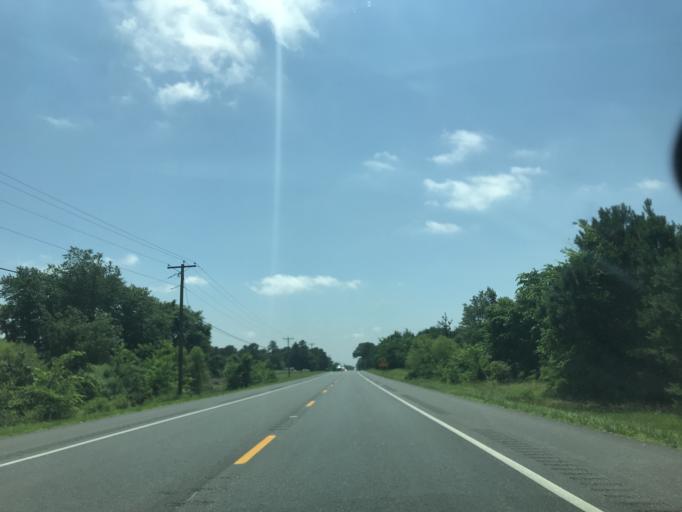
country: US
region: Maryland
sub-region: Dorchester County
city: Hurlock
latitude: 38.6148
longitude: -75.8912
